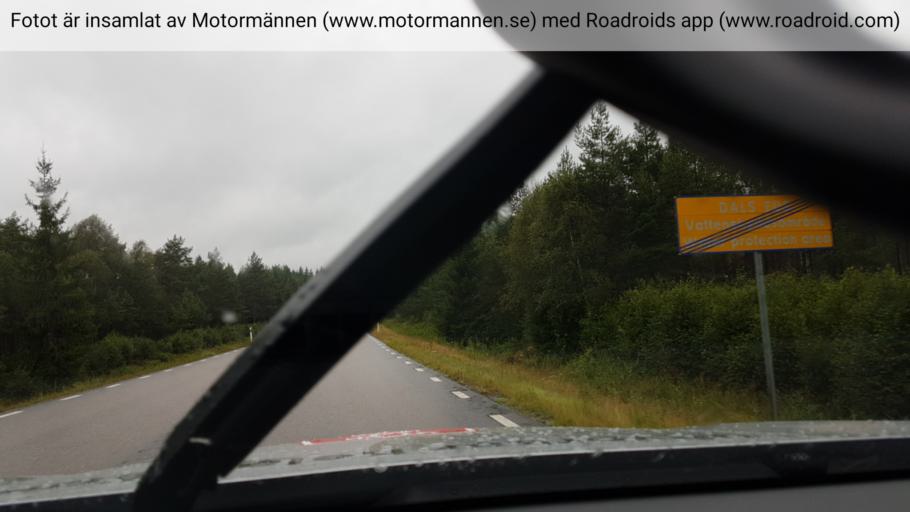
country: SE
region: Vaestra Goetaland
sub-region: Dals-Ed Kommun
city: Ed
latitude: 58.8935
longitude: 11.9263
